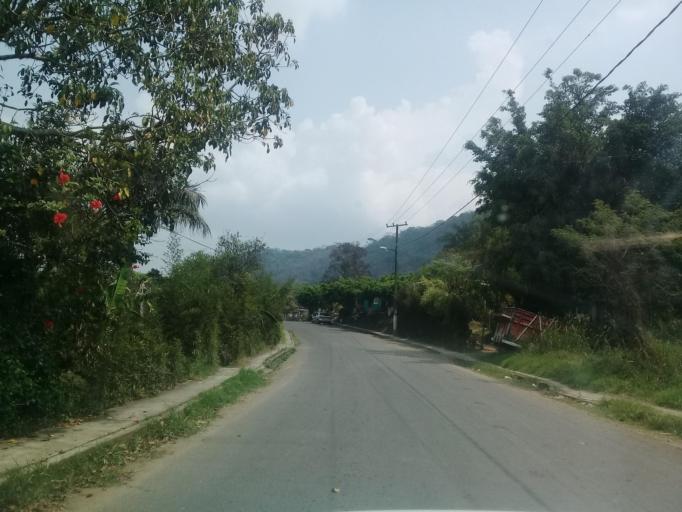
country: MX
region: Veracruz
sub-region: Cordoba
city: San Jose de Tapia
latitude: 18.8146
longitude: -96.9834
